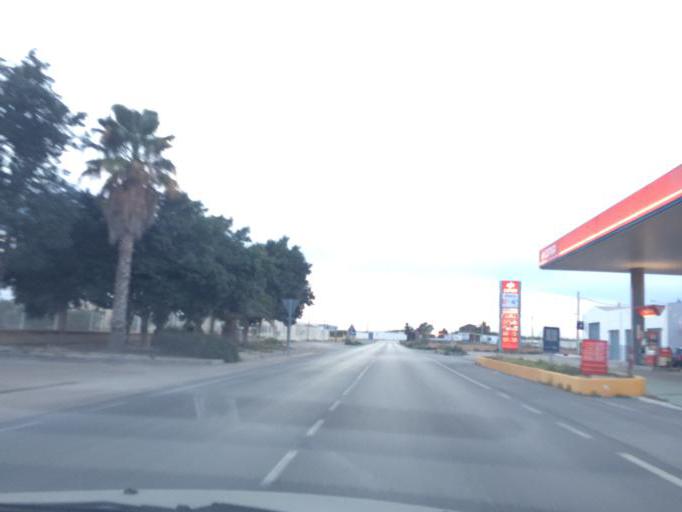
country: ES
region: Andalusia
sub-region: Provincia de Almeria
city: Viator
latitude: 36.8450
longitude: -2.3904
